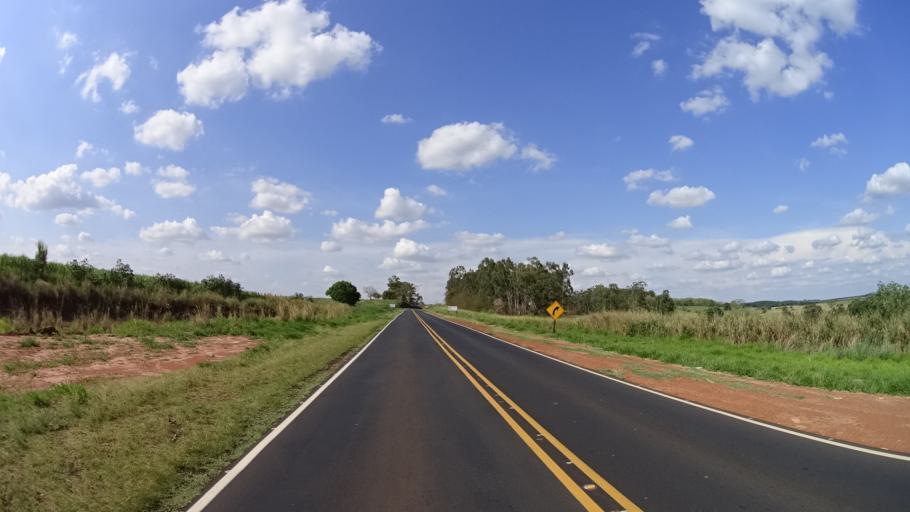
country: BR
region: Sao Paulo
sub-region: Urupes
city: Urupes
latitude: -21.0139
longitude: -49.2279
